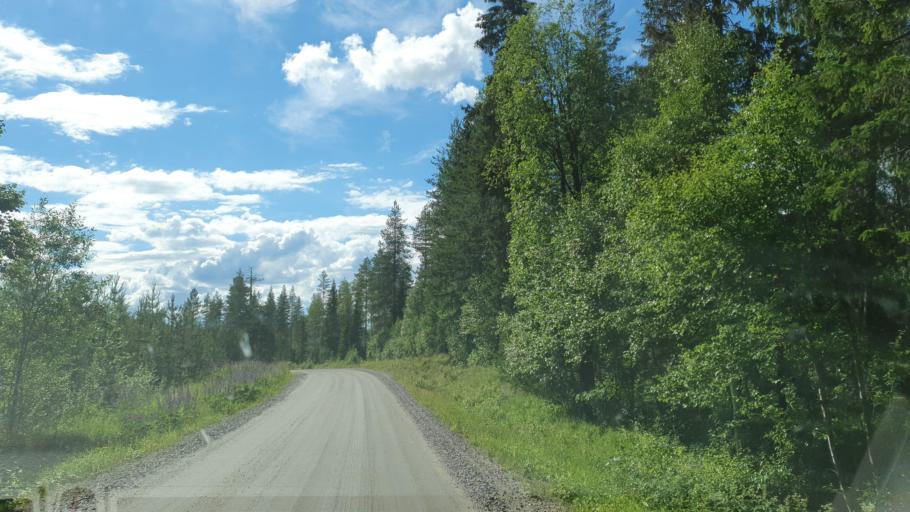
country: FI
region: Kainuu
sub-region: Kehys-Kainuu
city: Kuhmo
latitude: 64.1513
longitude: 29.7327
